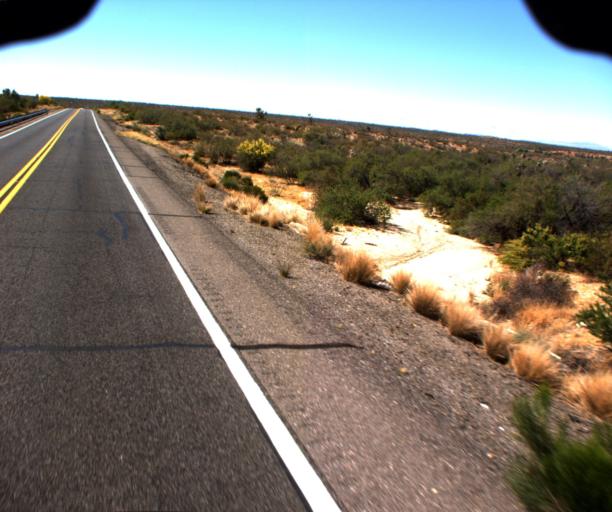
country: US
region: Arizona
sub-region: Yavapai County
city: Congress
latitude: 34.2117
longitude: -113.0660
